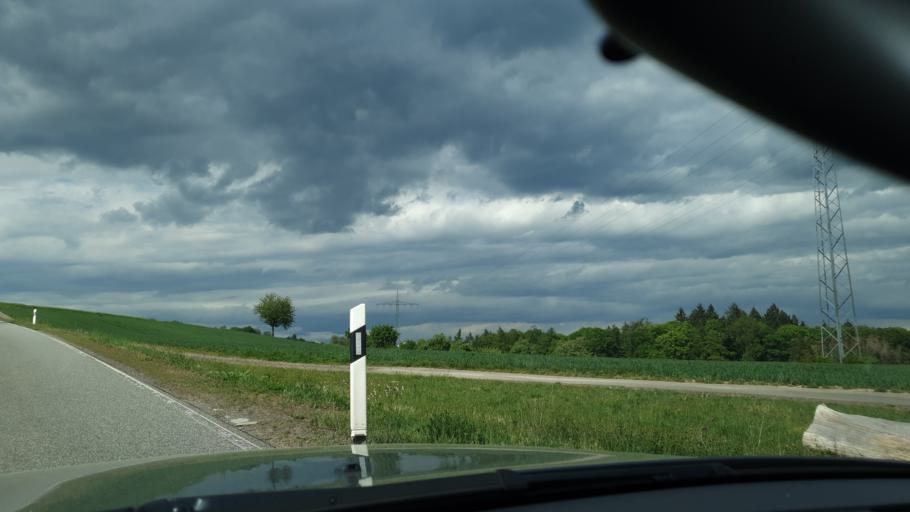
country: DE
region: Rheinland-Pfalz
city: Zweibrucken
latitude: 49.2749
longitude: 7.3770
